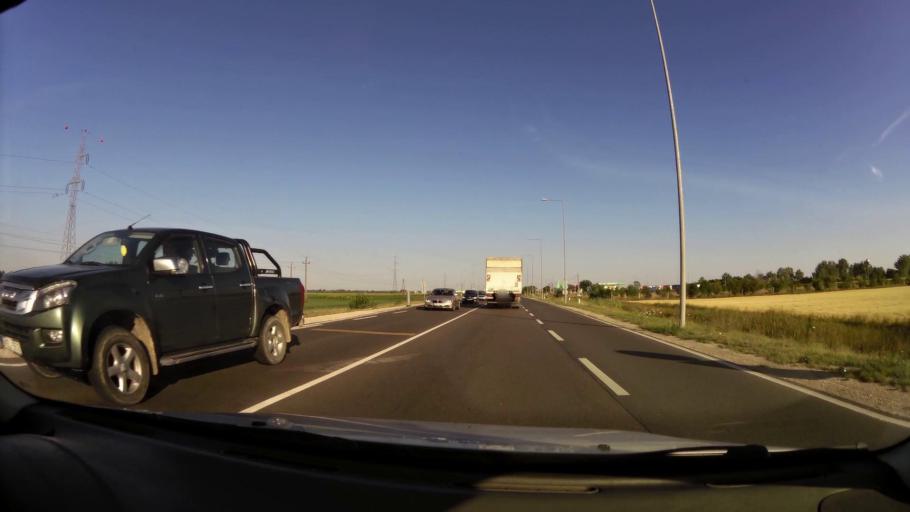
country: HU
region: Pest
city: Cegled
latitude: 47.2024
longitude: 19.7826
